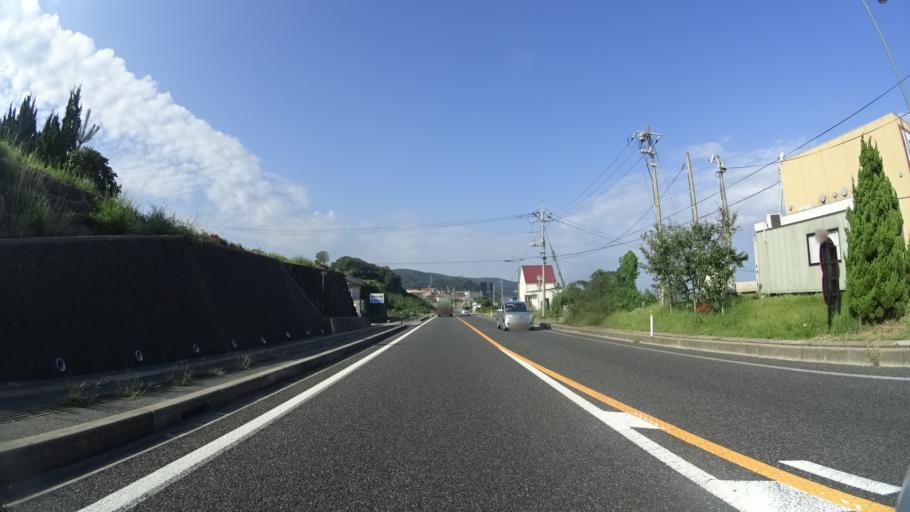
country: JP
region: Shimane
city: Izumo
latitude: 35.2897
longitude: 132.6318
